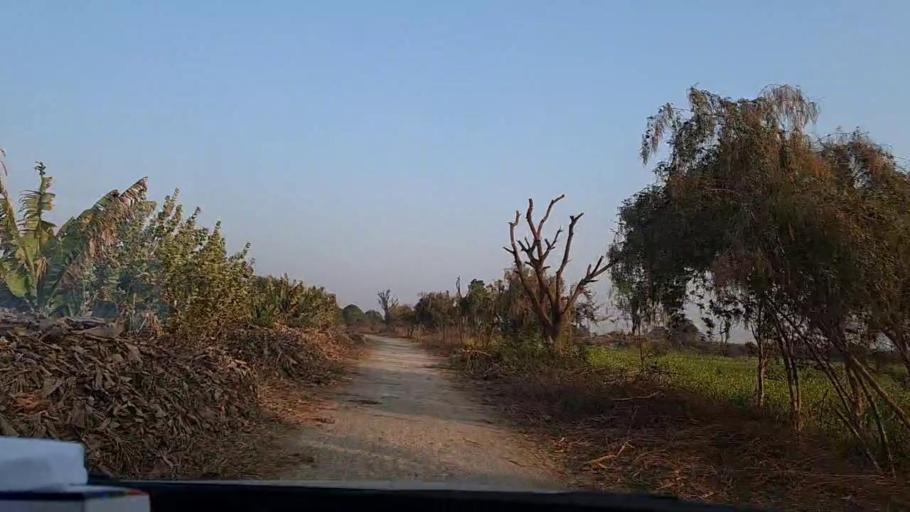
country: PK
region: Sindh
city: Tando Ghulam Ali
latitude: 25.1836
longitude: 68.9152
